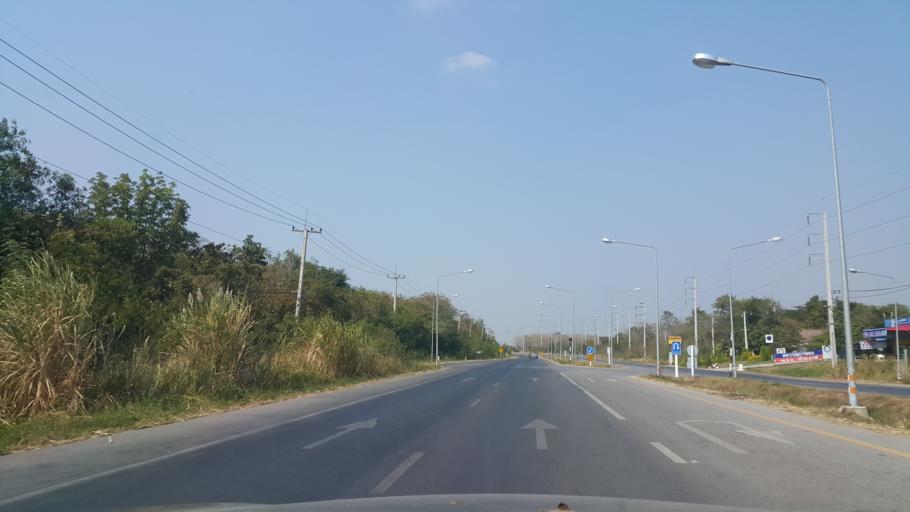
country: TH
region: Chaiyaphum
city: Phu Khiao
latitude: 16.4115
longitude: 102.1321
